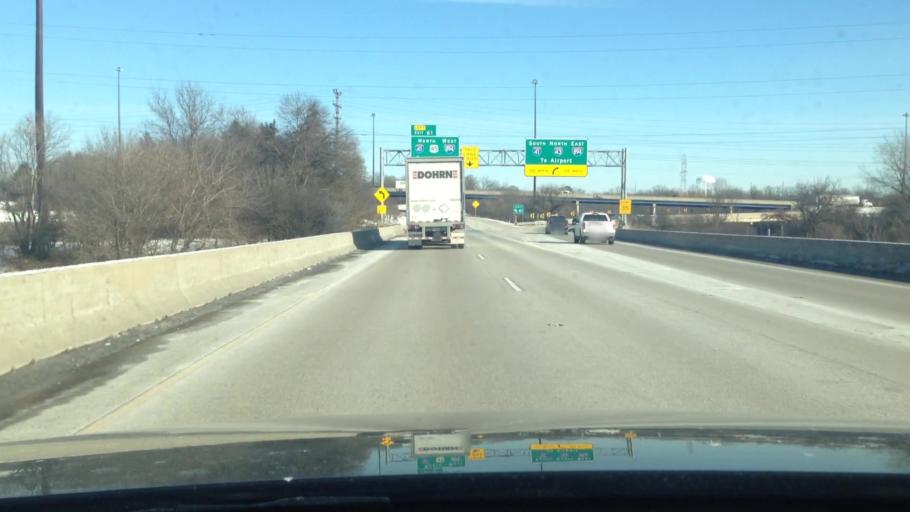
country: US
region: Wisconsin
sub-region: Milwaukee County
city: Hales Corners
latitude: 42.9607
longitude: -88.0398
